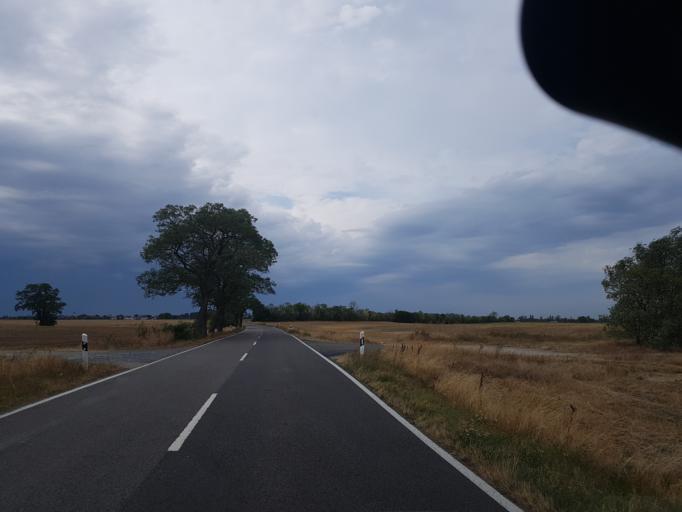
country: DE
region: Saxony
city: Strehla
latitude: 51.3918
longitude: 13.2726
